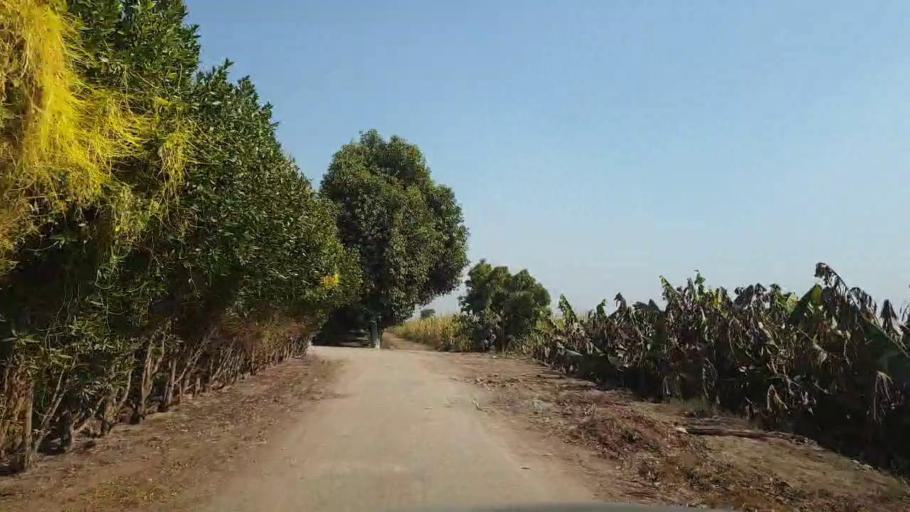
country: PK
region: Sindh
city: Tando Allahyar
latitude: 25.5558
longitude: 68.7088
